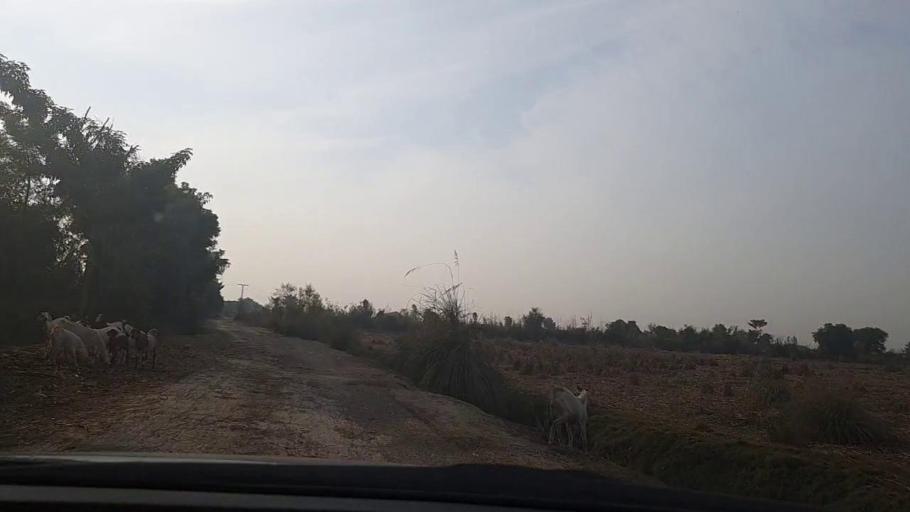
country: PK
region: Sindh
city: Daulatpur
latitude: 26.3347
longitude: 68.0533
